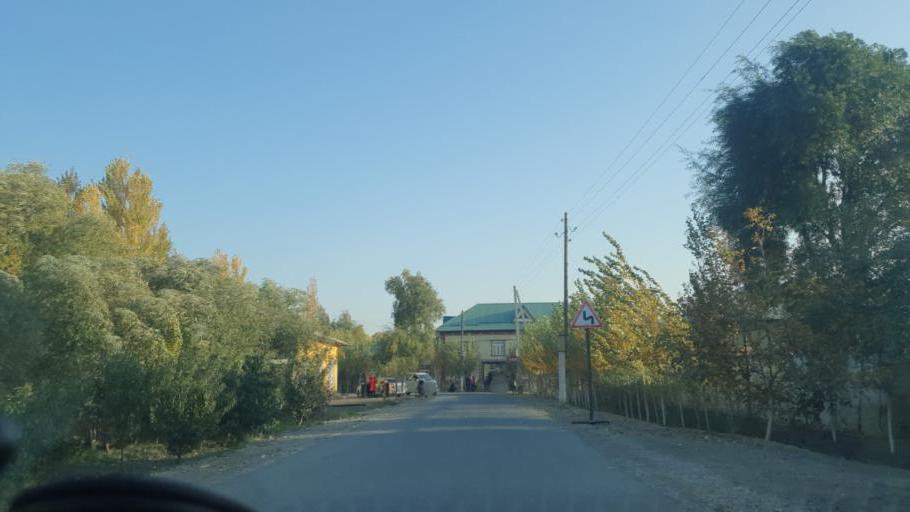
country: UZ
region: Fergana
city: Beshariq
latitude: 40.4626
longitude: 70.5437
